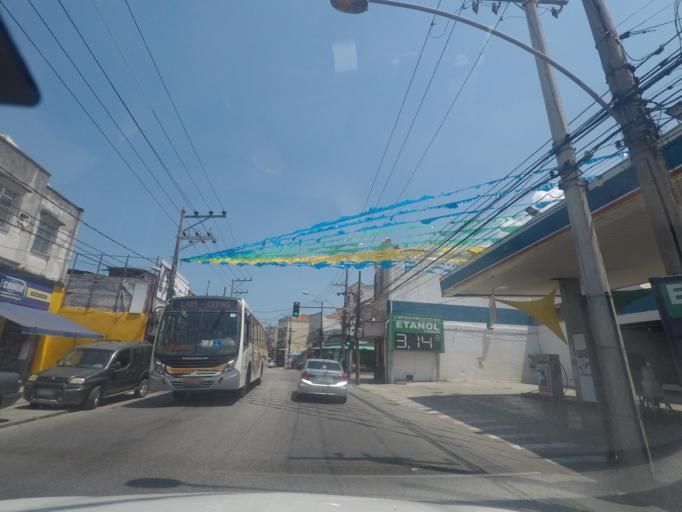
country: BR
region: Rio de Janeiro
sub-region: Duque De Caxias
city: Duque de Caxias
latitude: -22.8484
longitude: -43.2670
